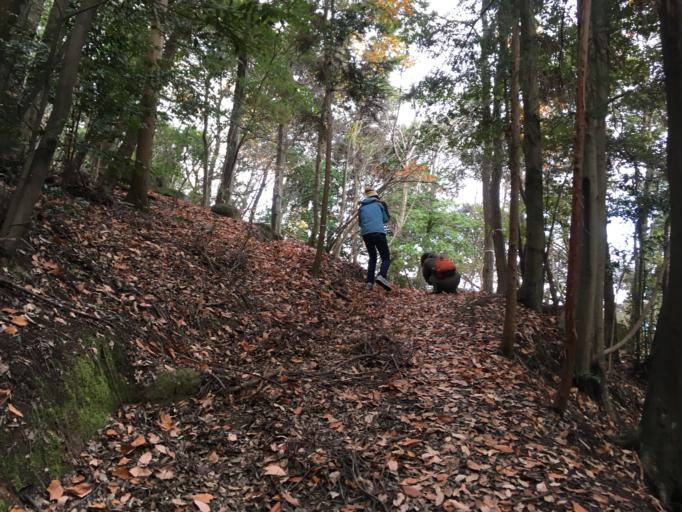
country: JP
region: Nara
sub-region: Ikoma-shi
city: Ikoma
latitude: 34.6908
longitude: 135.6894
